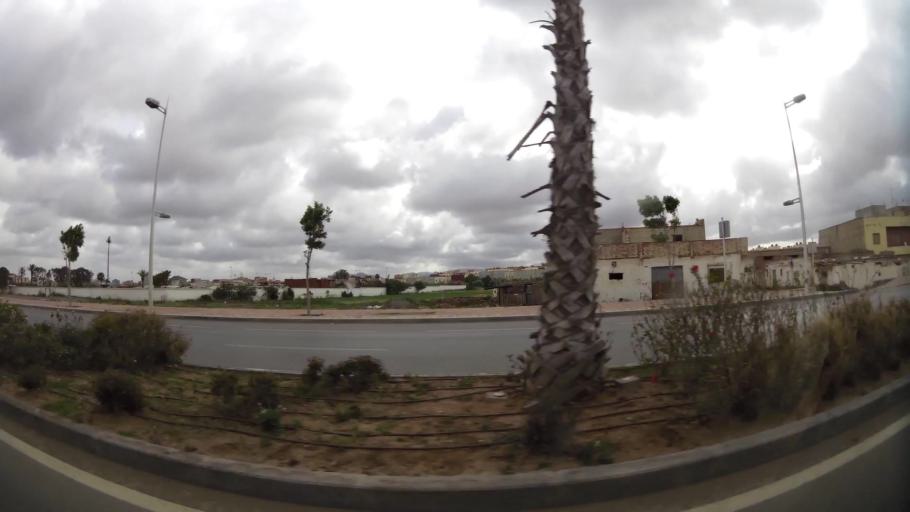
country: MA
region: Oriental
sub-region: Nador
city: Nador
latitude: 35.1633
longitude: -2.9098
